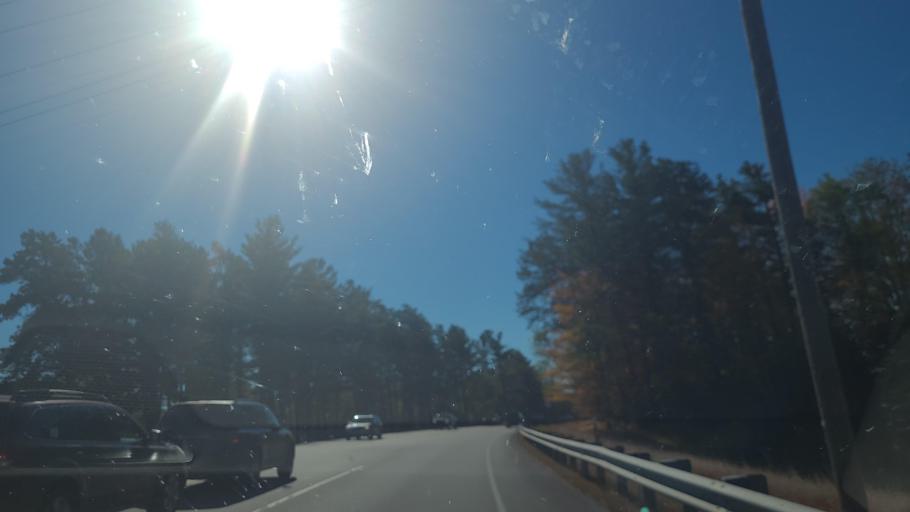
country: US
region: New Hampshire
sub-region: Carroll County
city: Conway
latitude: 44.0052
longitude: -71.0887
